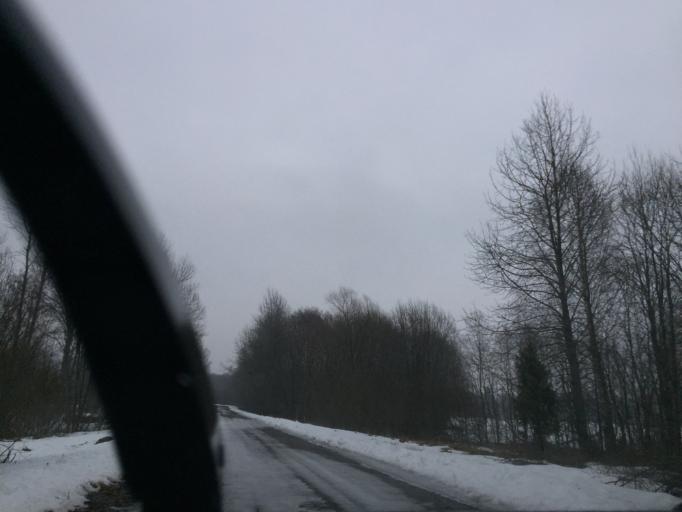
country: EE
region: Laeaene
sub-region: Lihula vald
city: Lihula
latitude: 58.6255
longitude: 23.6757
